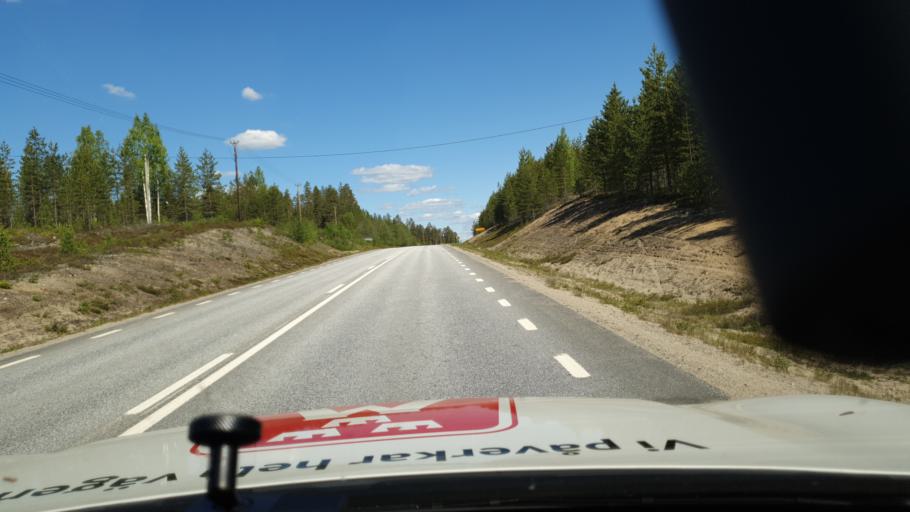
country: SE
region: Vaesterbotten
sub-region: Vannas Kommun
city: Vaennaes
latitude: 64.0292
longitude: 19.6926
